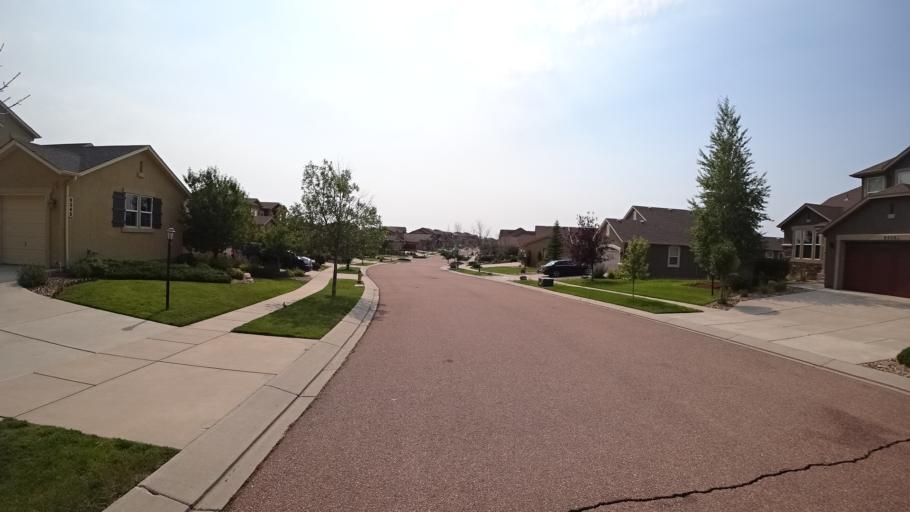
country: US
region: Colorado
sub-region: El Paso County
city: Black Forest
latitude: 38.9676
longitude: -104.7321
